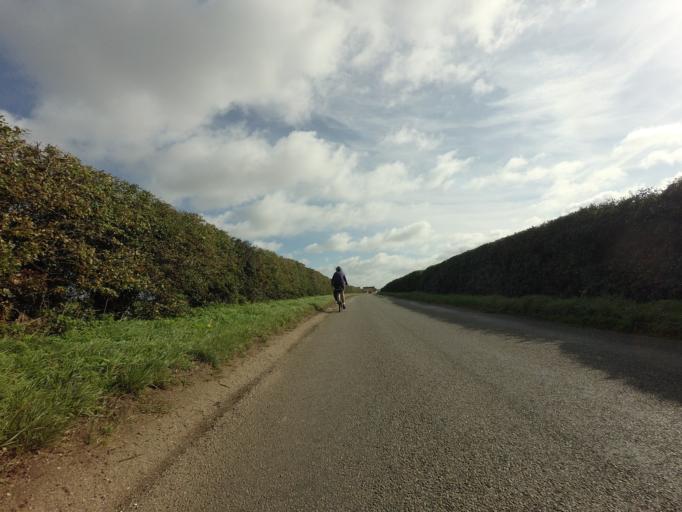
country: GB
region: England
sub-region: Norfolk
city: Wells-next-the-Sea
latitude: 52.9115
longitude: 0.7156
